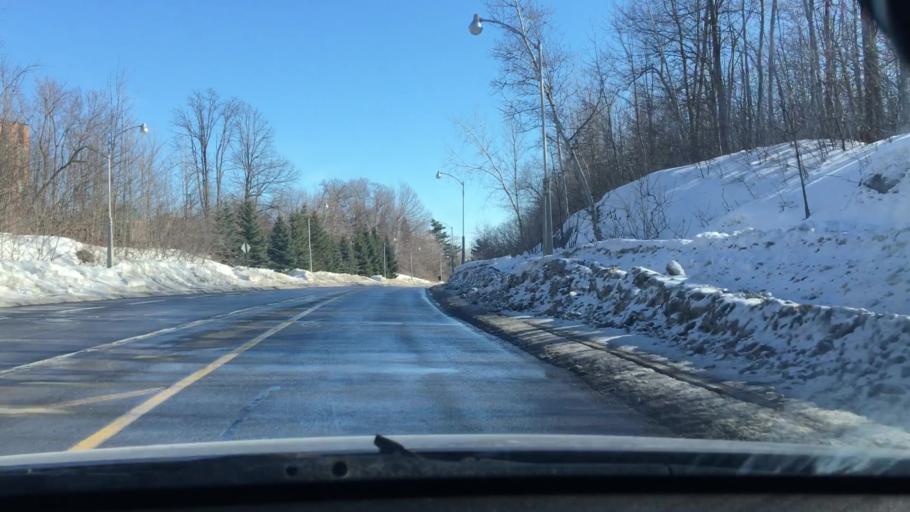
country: CA
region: Ontario
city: Ottawa
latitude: 45.4456
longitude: -75.6410
